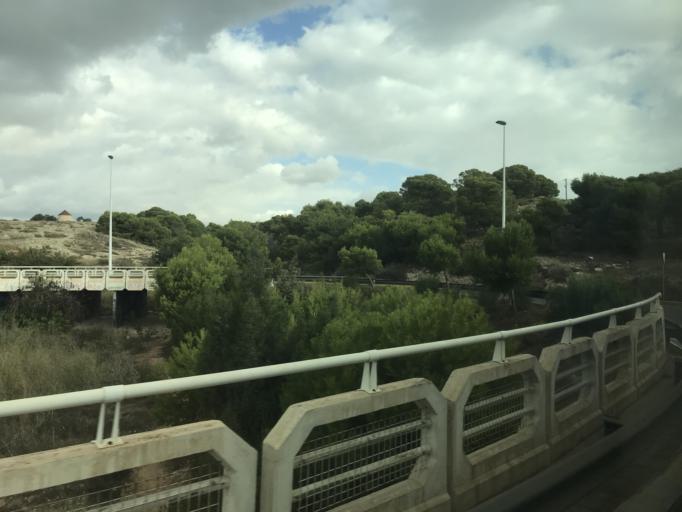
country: ES
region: Valencia
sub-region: Provincia de Alicante
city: Santa Pola
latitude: 38.1999
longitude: -0.5603
